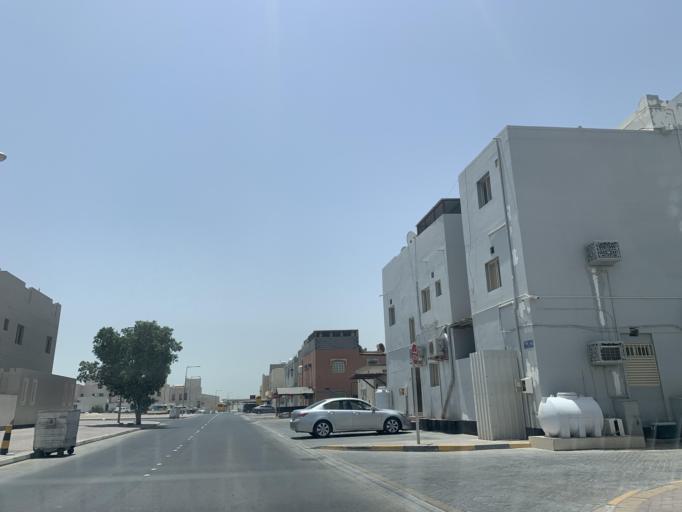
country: BH
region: Northern
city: Sitrah
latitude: 26.1597
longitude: 50.6232
